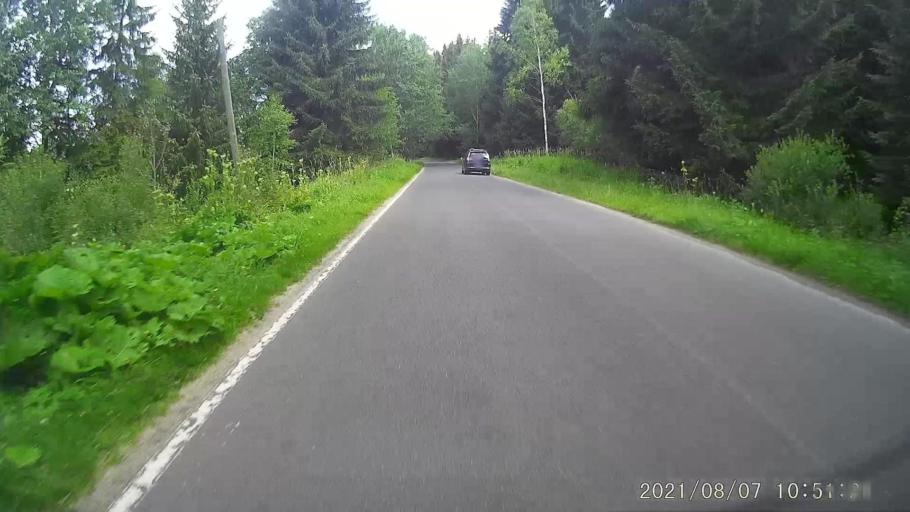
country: PL
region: Lower Silesian Voivodeship
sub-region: Powiat klodzki
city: Polanica-Zdroj
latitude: 50.2899
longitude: 16.4685
